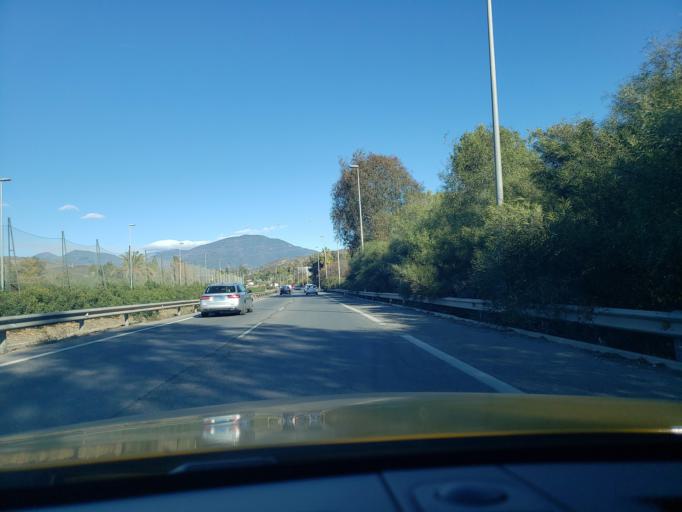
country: ES
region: Andalusia
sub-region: Provincia de Malaga
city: Marbella
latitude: 36.5020
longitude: -4.9471
